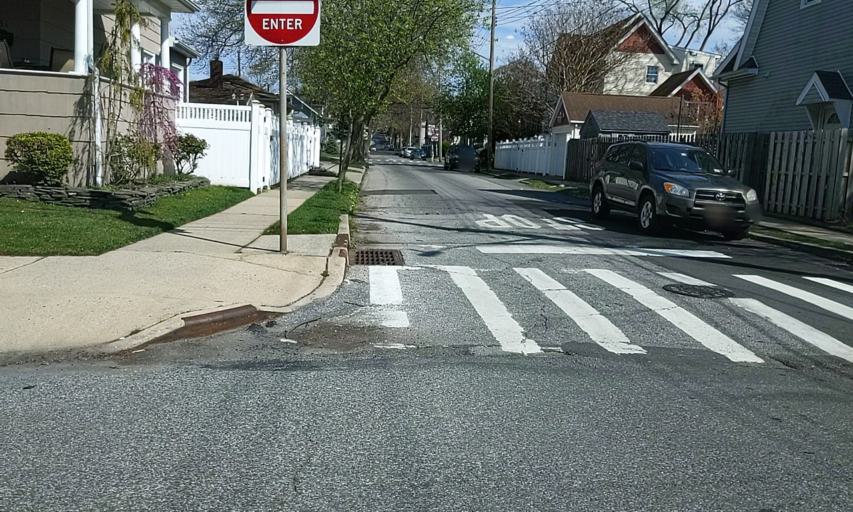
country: US
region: New York
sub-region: Richmond County
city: Bloomfield
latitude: 40.6178
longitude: -74.1394
